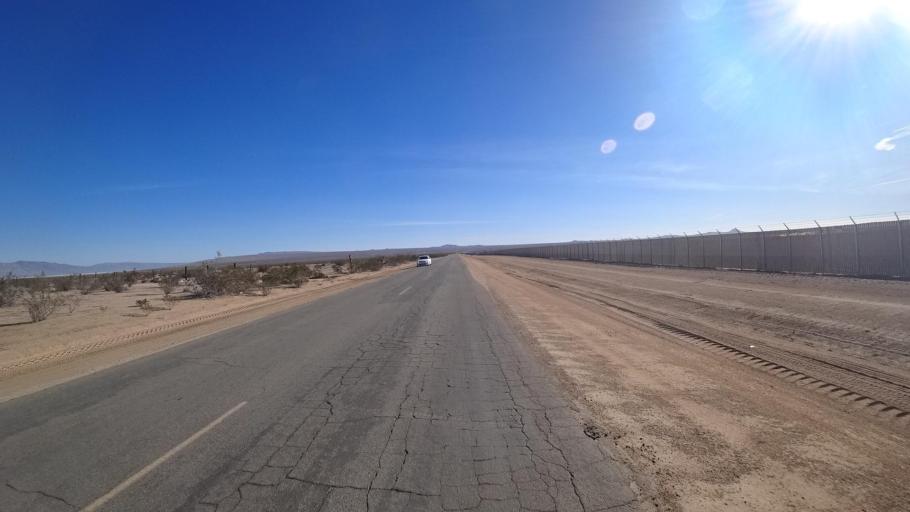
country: US
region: California
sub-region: Kern County
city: California City
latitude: 35.1987
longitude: -117.9975
